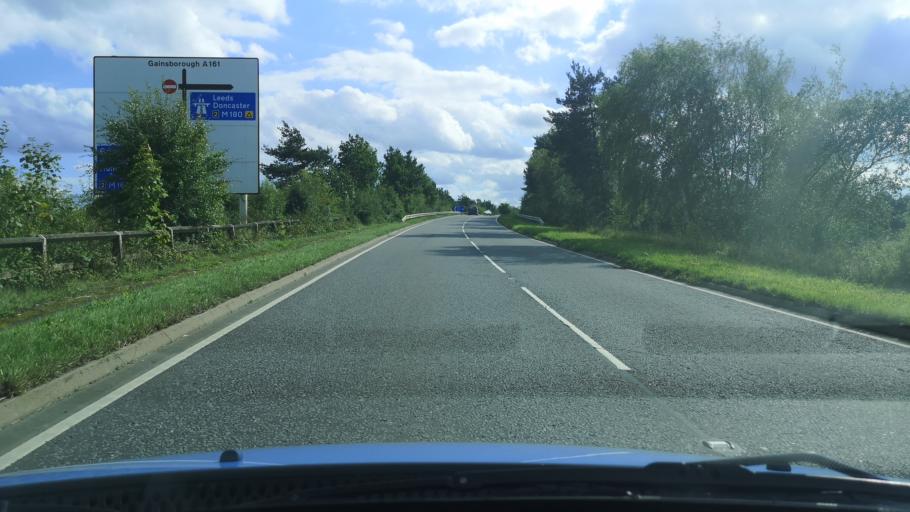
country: GB
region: England
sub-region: North Lincolnshire
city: Belton
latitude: 53.5719
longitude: -0.8176
